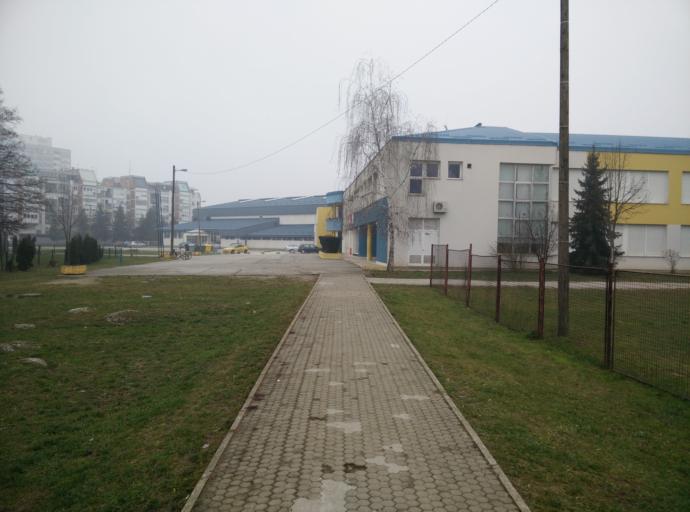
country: HR
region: Karlovacka
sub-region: Grad Karlovac
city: Karlovac
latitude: 45.4840
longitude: 15.5505
